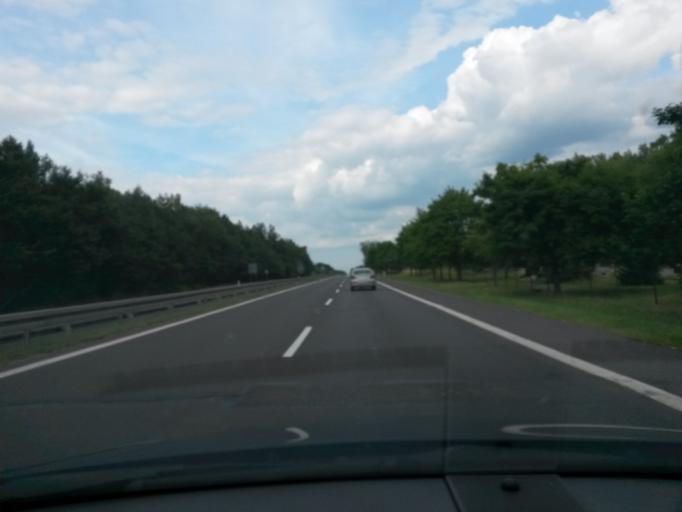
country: PL
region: Lodz Voivodeship
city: Zabia Wola
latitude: 52.0463
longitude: 20.7079
